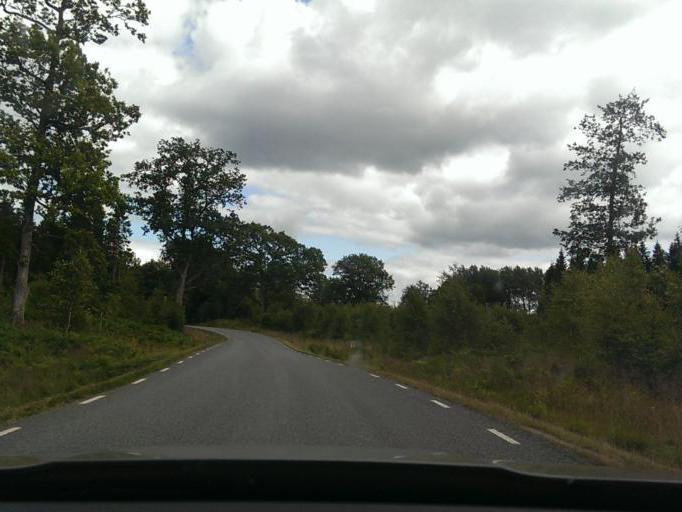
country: SE
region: Kronoberg
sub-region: Ljungby Kommun
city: Lagan
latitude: 57.0140
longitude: 13.9166
